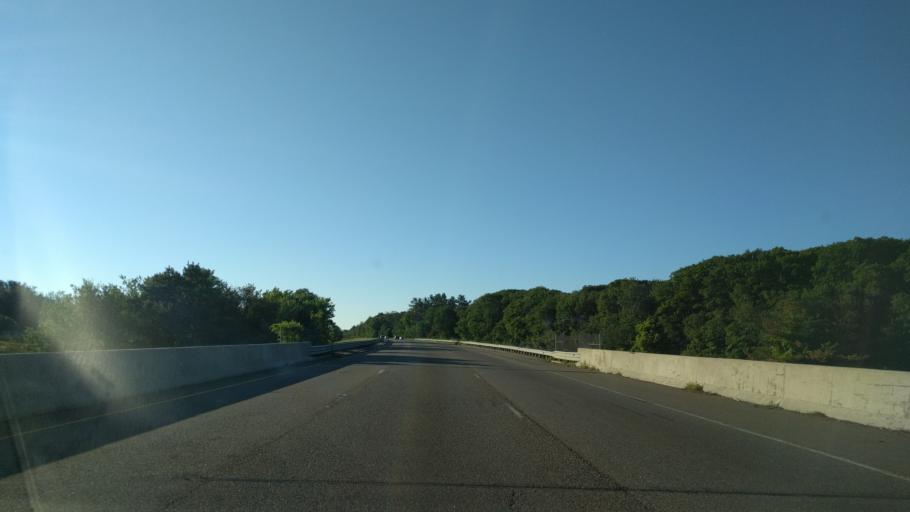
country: US
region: Massachusetts
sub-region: Norfolk County
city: Franklin
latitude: 42.0649
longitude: -71.4017
